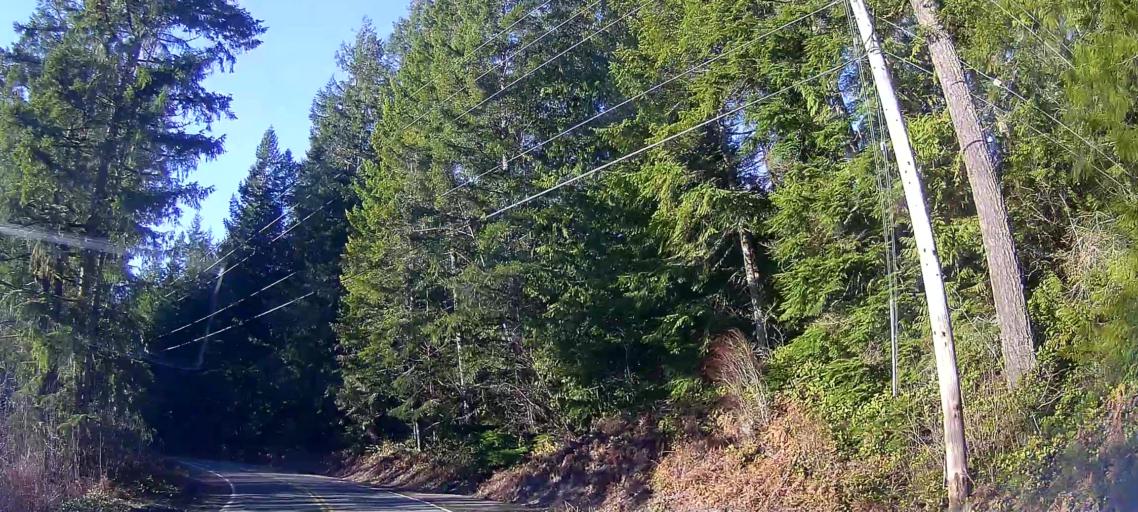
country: US
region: Washington
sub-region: Snohomish County
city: Darrington
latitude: 48.5727
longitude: -121.7704
